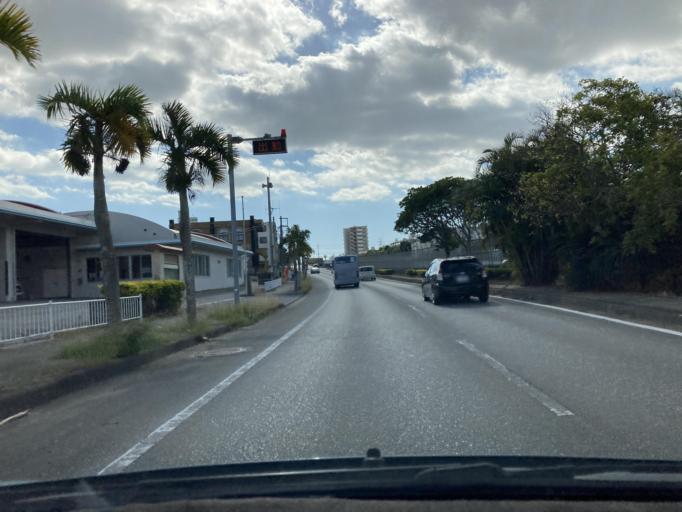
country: JP
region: Okinawa
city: Okinawa
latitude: 26.3295
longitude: 127.7849
